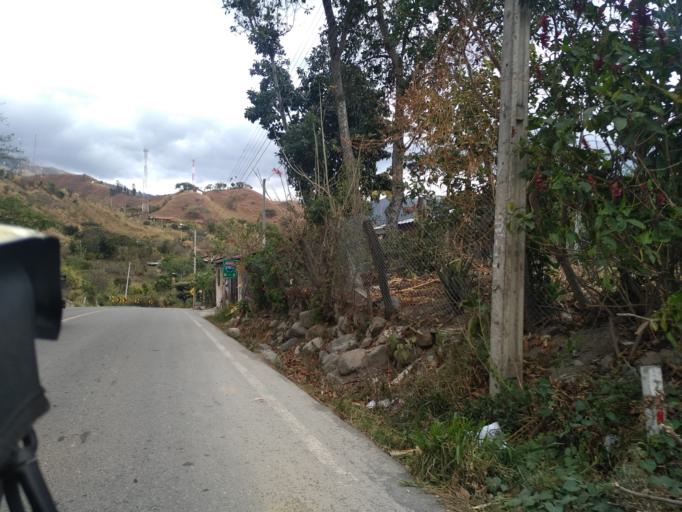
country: EC
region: Loja
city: Loja
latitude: -4.2325
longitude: -79.2324
